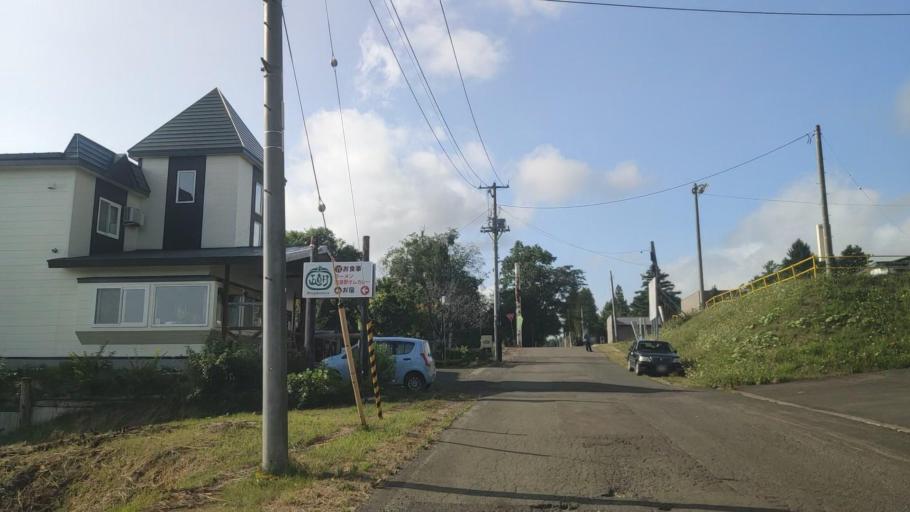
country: JP
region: Hokkaido
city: Shimo-furano
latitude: 43.3441
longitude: 142.3629
